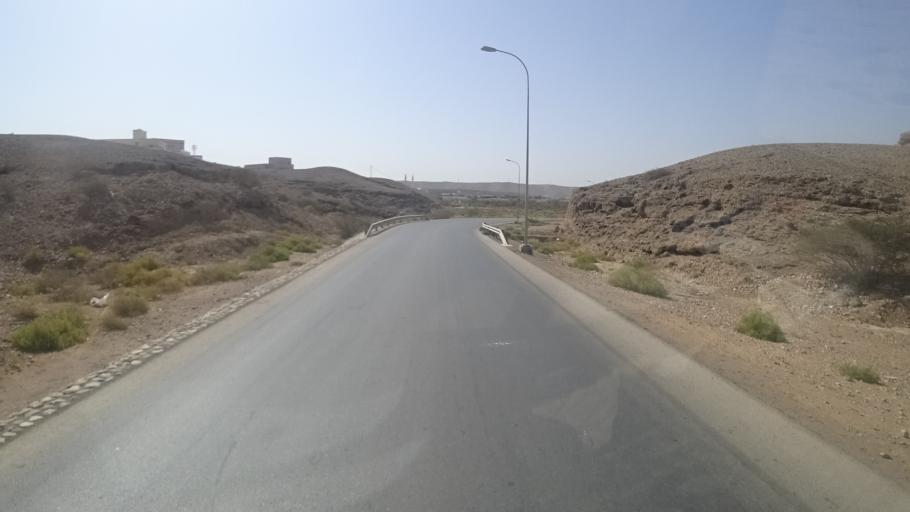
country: OM
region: Ash Sharqiyah
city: Sur
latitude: 22.5423
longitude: 59.4963
